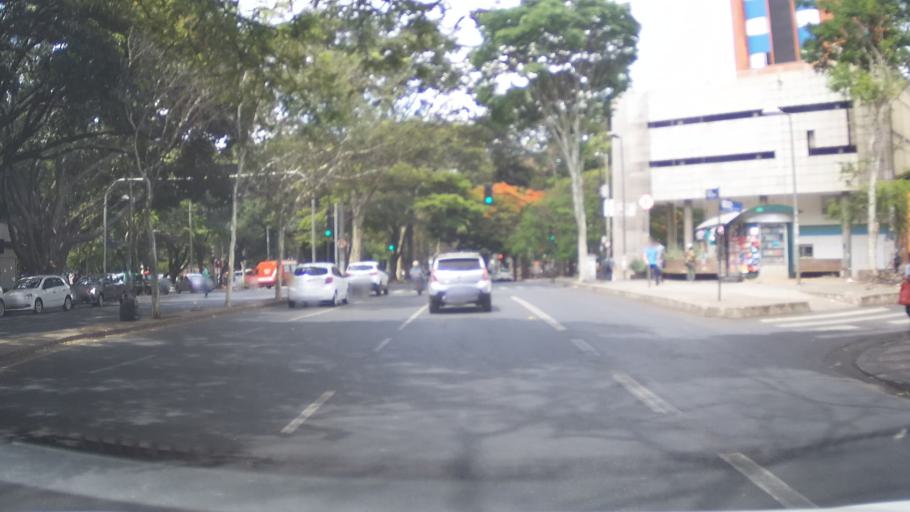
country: BR
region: Minas Gerais
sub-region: Belo Horizonte
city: Belo Horizonte
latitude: -19.9249
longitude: -43.9284
